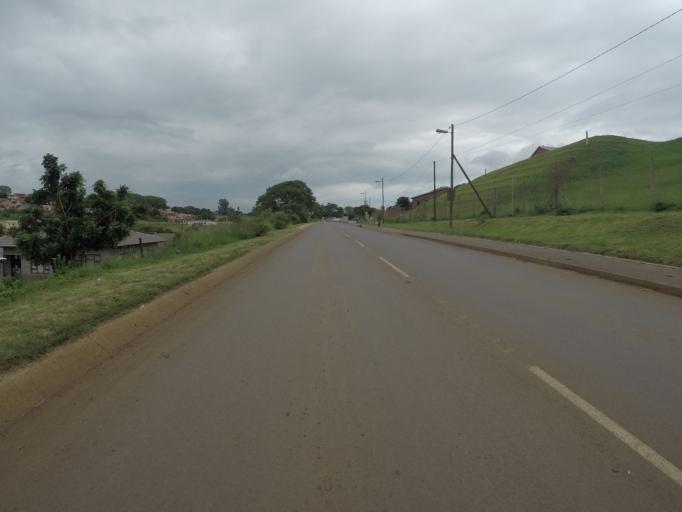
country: ZA
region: KwaZulu-Natal
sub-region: uThungulu District Municipality
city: Empangeni
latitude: -28.7795
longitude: 31.8636
